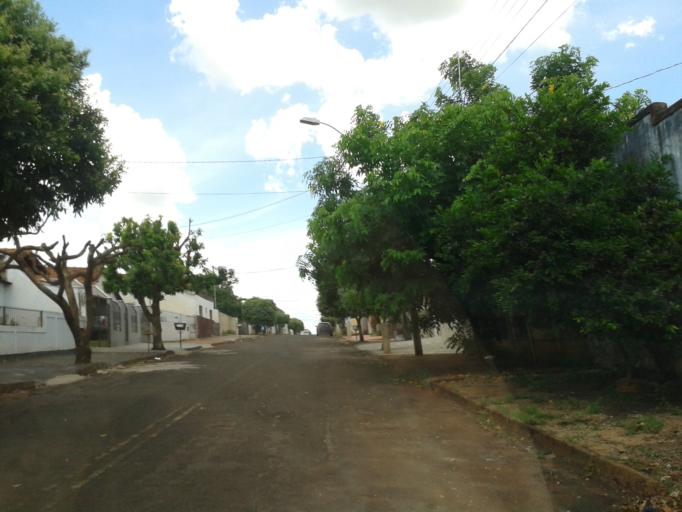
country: BR
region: Minas Gerais
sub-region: Ituiutaba
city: Ituiutaba
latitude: -18.9838
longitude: -49.4721
